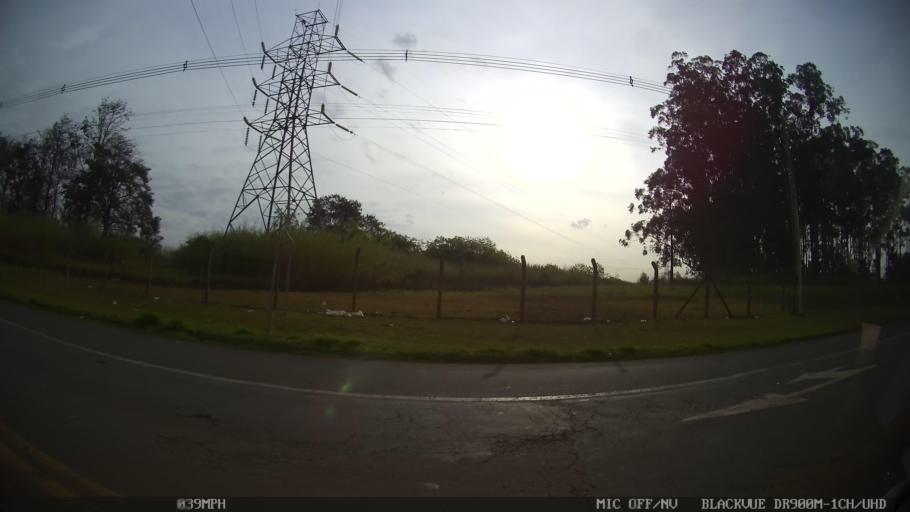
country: BR
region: Sao Paulo
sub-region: Piracicaba
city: Piracicaba
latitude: -22.7206
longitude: -47.5835
